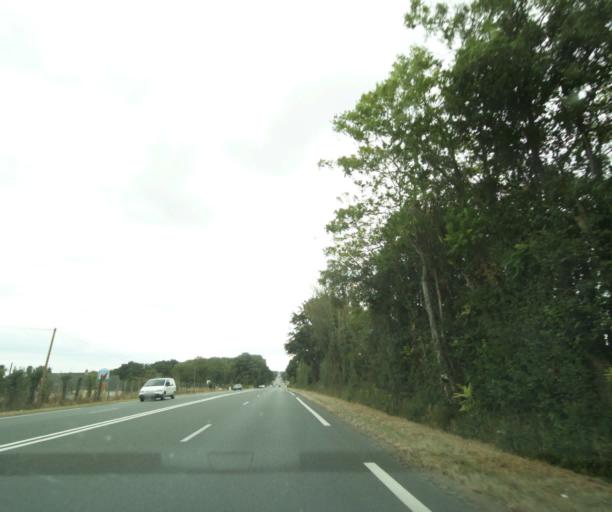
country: FR
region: Pays de la Loire
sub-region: Departement de Maine-et-Loire
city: Pellouailles-les-Vignes
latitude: 47.5060
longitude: -0.4764
